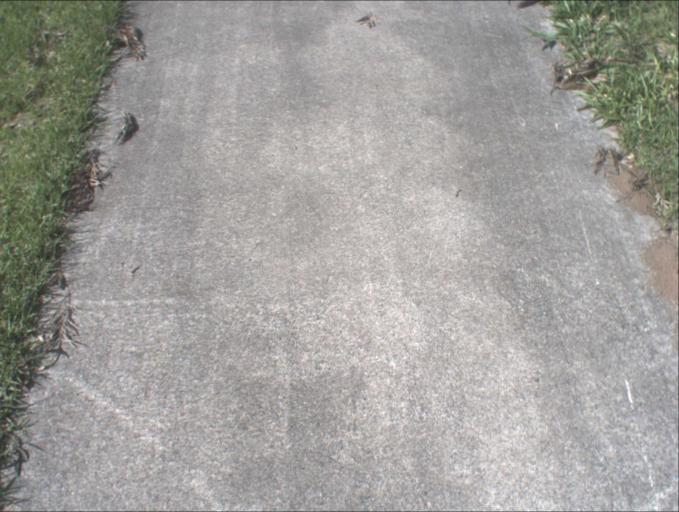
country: AU
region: Queensland
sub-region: Logan
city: Chambers Flat
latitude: -27.7596
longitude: 153.0912
